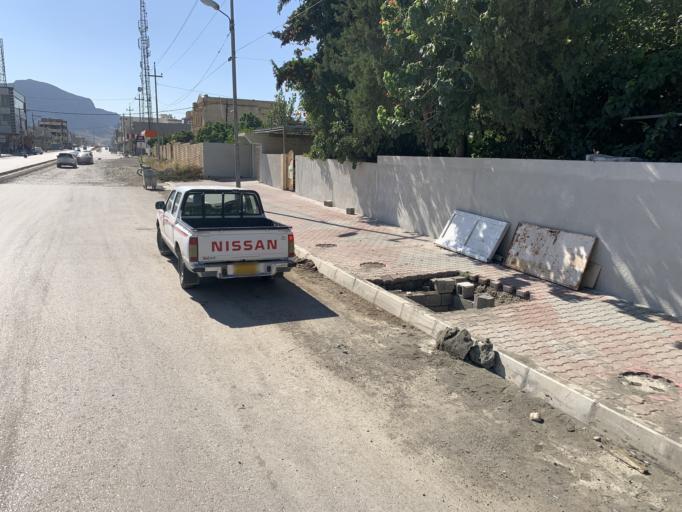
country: IQ
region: As Sulaymaniyah
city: Raniye
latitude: 36.2566
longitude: 44.8781
